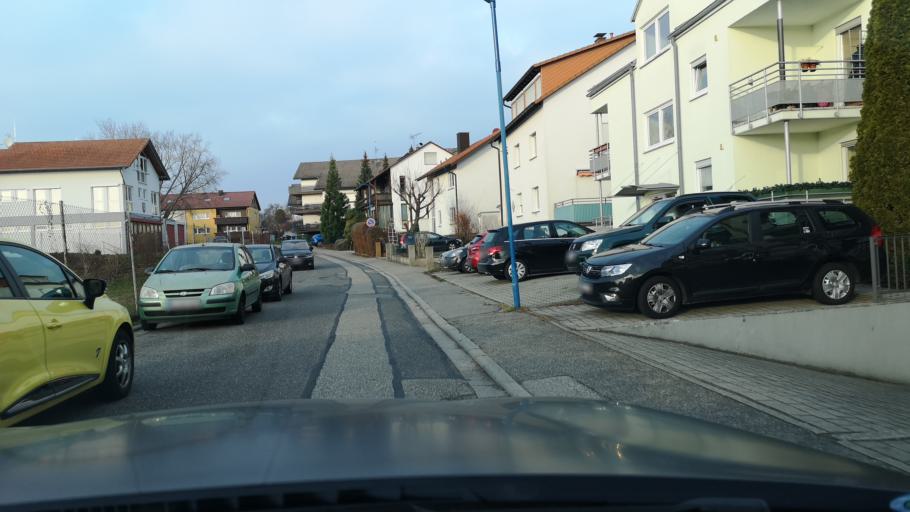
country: DE
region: Baden-Wuerttemberg
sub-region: Karlsruhe Region
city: Ettlingen
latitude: 48.9338
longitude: 8.4646
